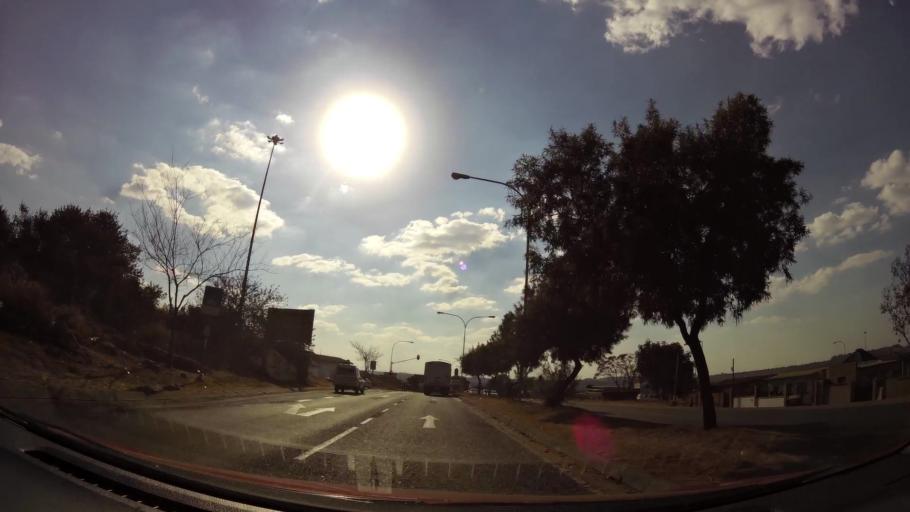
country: ZA
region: Gauteng
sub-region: City of Johannesburg Metropolitan Municipality
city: Soweto
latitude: -26.2298
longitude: 27.8733
